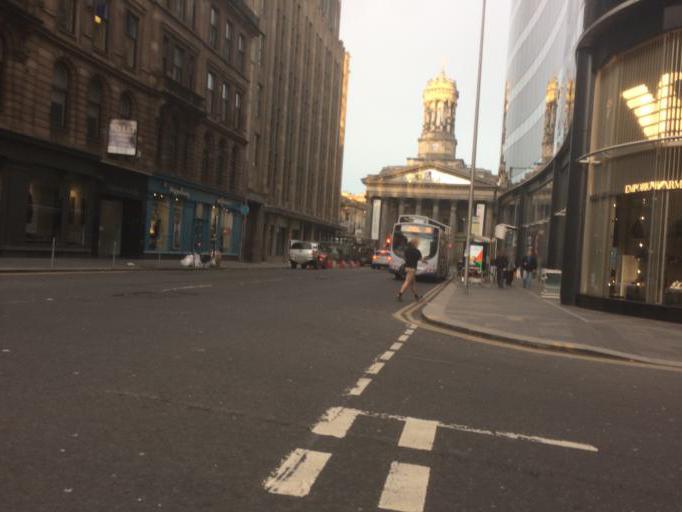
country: GB
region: Scotland
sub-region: Glasgow City
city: Glasgow
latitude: 55.8600
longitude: -4.2505
